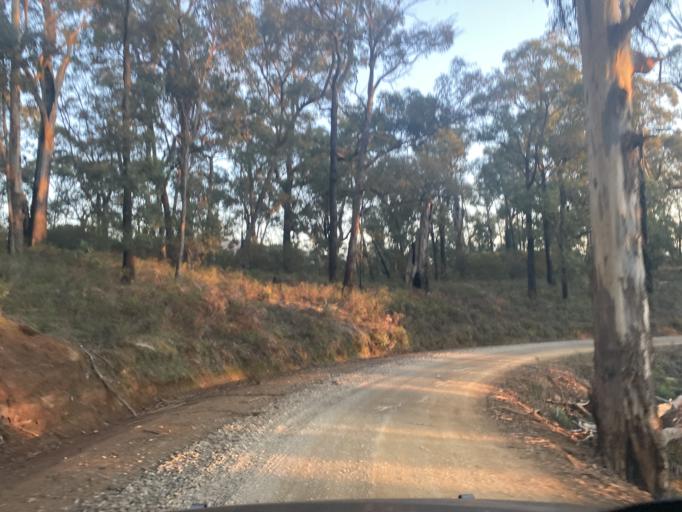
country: AU
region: Victoria
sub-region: Yarra Ranges
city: Healesville
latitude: -37.4255
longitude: 145.5155
